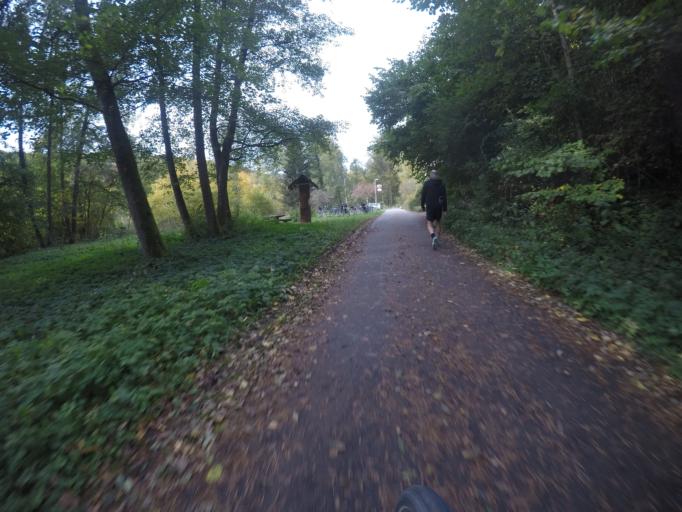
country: DE
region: Baden-Wuerttemberg
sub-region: Tuebingen Region
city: Tuebingen
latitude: 48.5407
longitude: 9.0776
